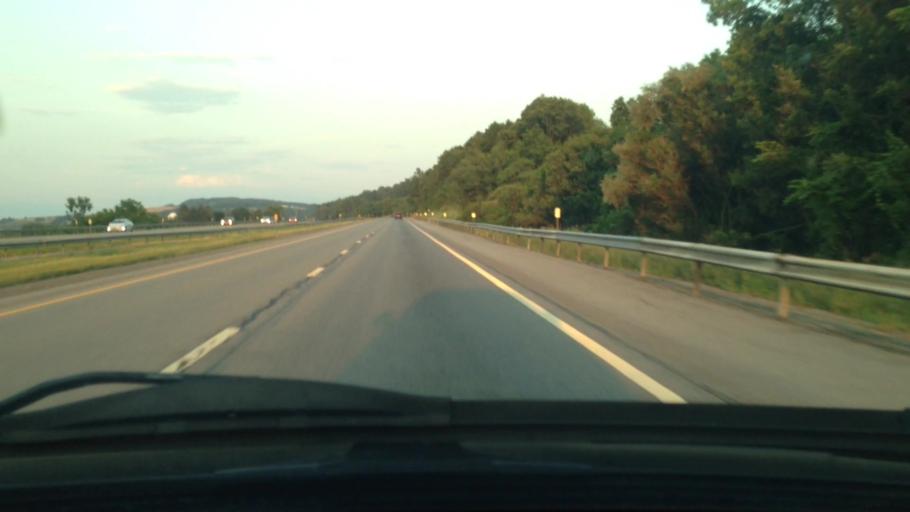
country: US
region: New York
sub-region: Herkimer County
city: Little Falls
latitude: 43.0092
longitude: -74.9103
